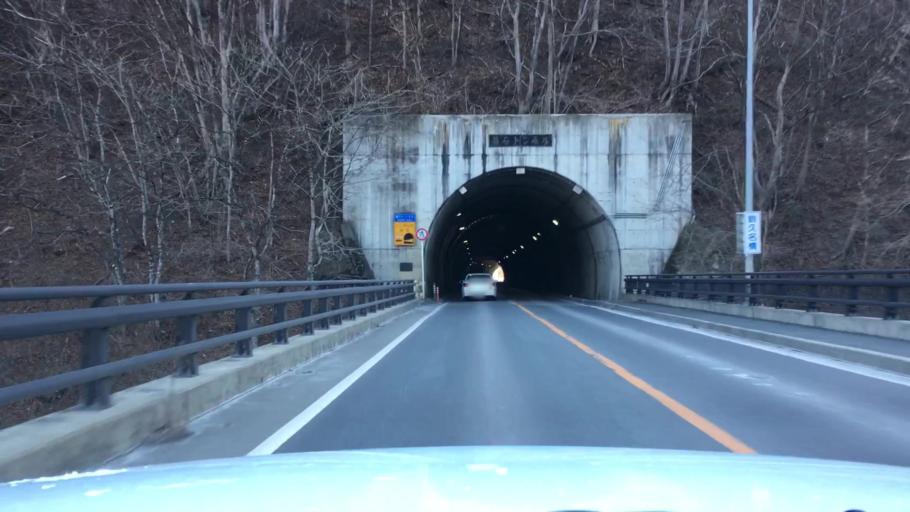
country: JP
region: Iwate
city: Tono
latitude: 39.6224
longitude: 141.6157
